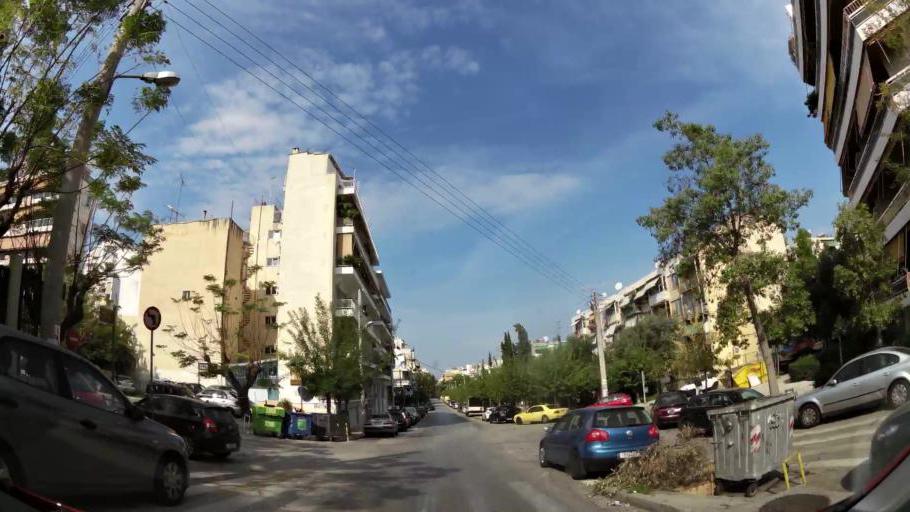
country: GR
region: Attica
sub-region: Nomarchia Athinas
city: Nea Smyrni
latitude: 37.9529
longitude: 23.7178
